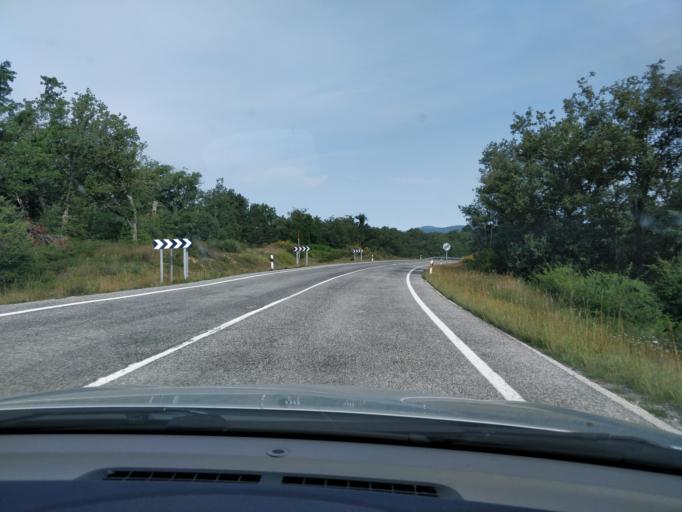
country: ES
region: Cantabria
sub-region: Provincia de Cantabria
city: San Pedro del Romeral
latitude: 42.9598
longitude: -3.7740
